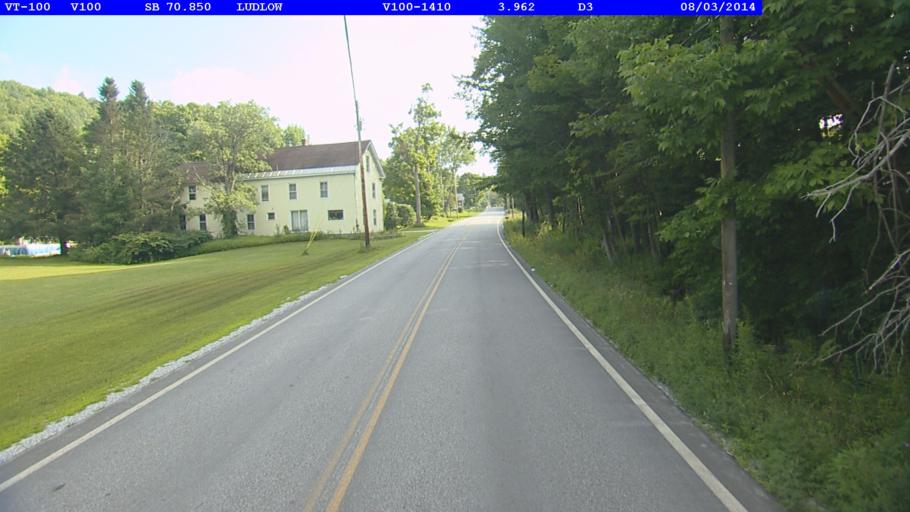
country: US
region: Vermont
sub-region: Windsor County
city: Chester
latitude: 43.3825
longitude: -72.7114
